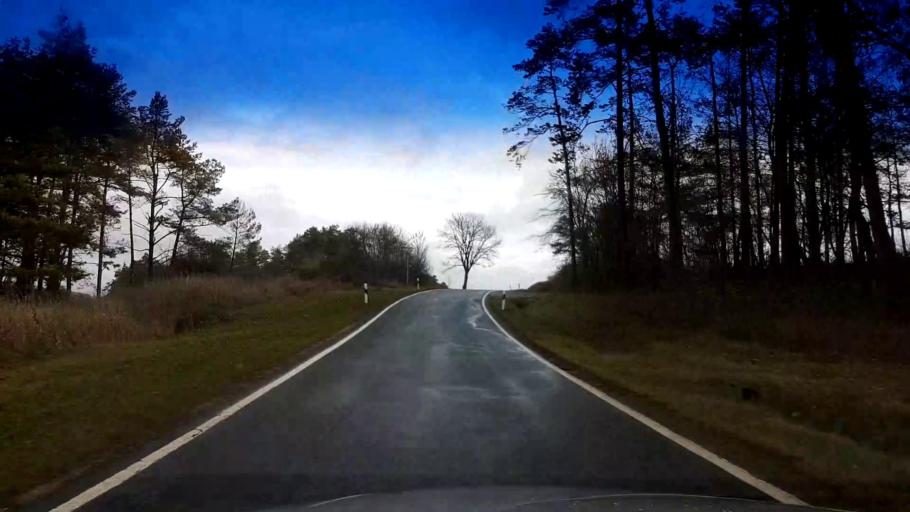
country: DE
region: Bavaria
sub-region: Upper Franconia
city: Poxdorf
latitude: 49.9228
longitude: 11.1121
